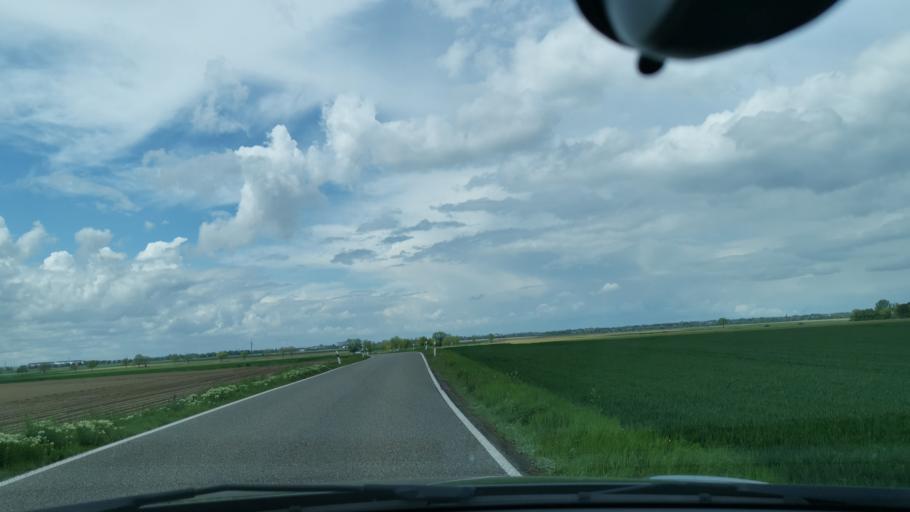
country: DE
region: North Rhine-Westphalia
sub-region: Regierungsbezirk Dusseldorf
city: Neubrueck
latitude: 51.0887
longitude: 6.6609
